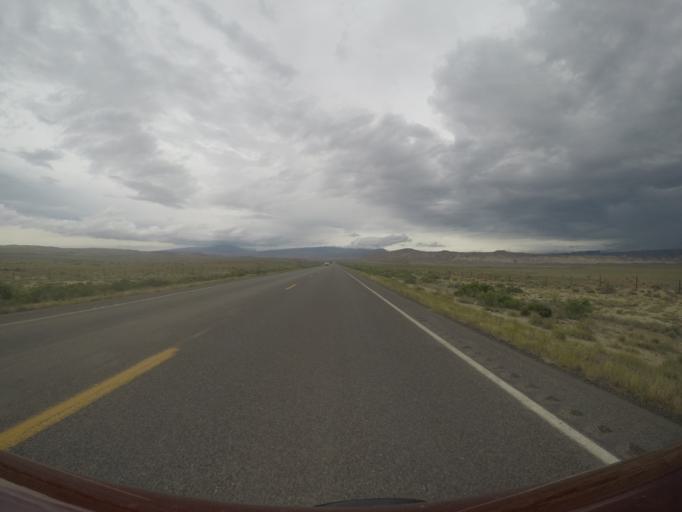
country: US
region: Wyoming
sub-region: Big Horn County
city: Lovell
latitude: 44.8946
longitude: -108.2890
